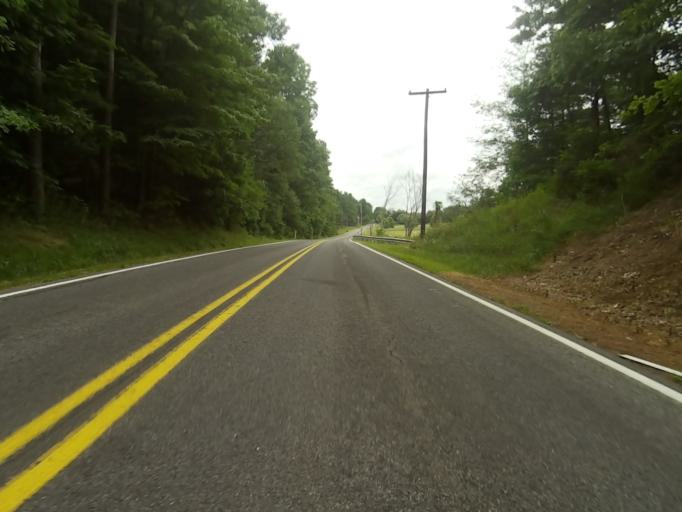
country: US
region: Pennsylvania
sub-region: Centre County
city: Pine Grove Mills
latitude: 40.7431
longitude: -77.9576
